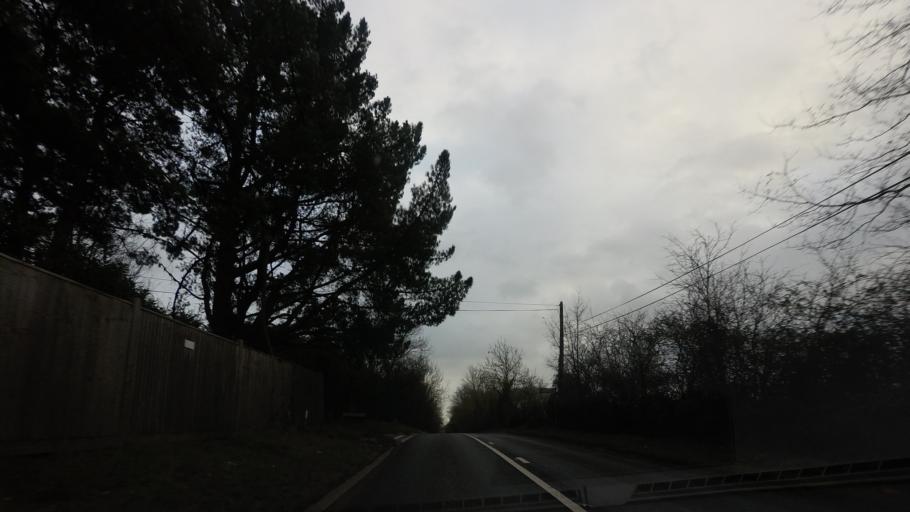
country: GB
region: England
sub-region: Kent
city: East Peckham
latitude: 51.2373
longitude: 0.3809
